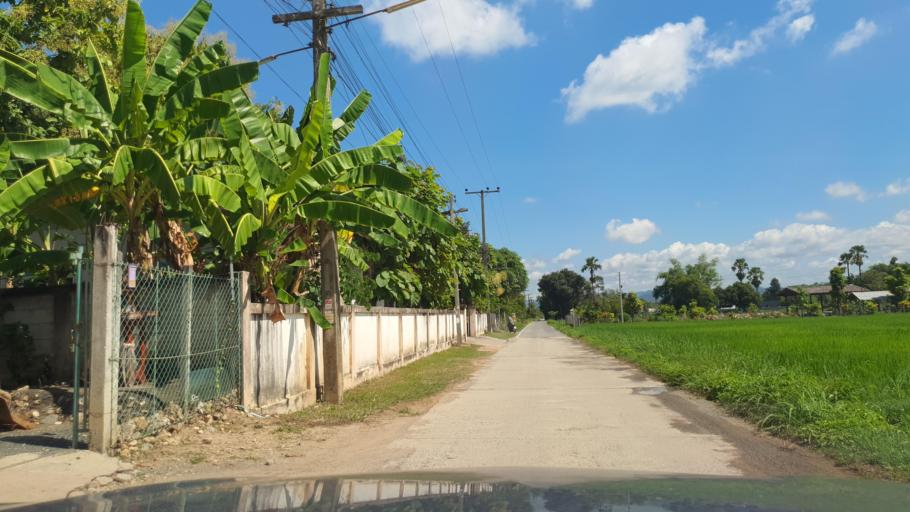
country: TH
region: Chiang Mai
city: San Kamphaeng
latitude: 18.7667
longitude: 99.1693
